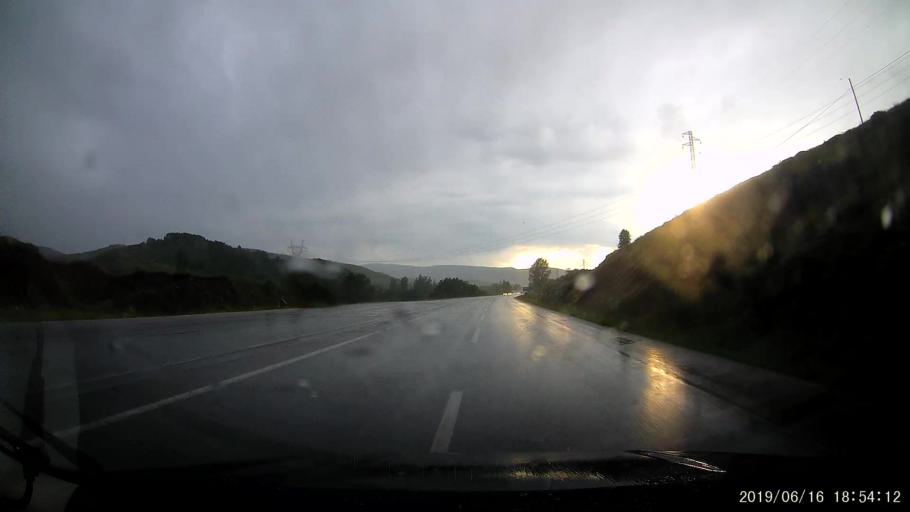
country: TR
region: Erzincan
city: Catalcam
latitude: 39.8964
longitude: 38.8590
